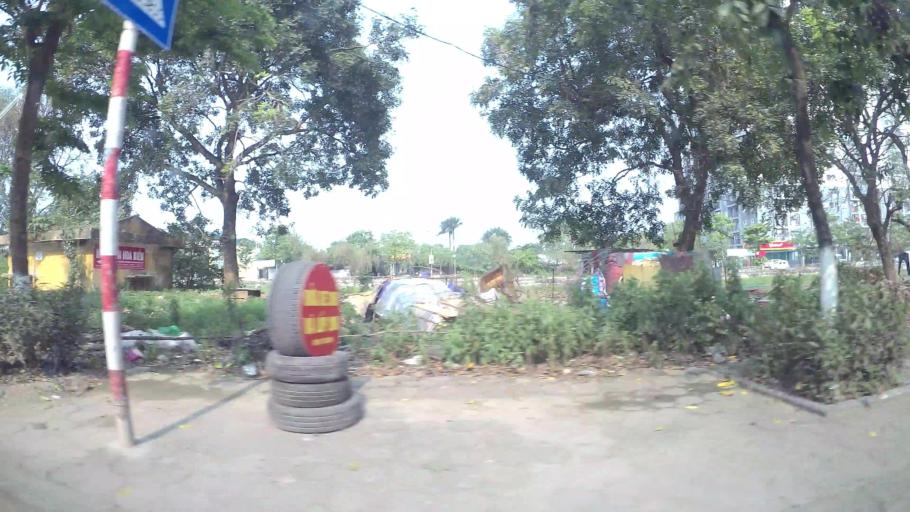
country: VN
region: Ha Noi
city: Thanh Xuan
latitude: 20.9756
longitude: 105.8249
